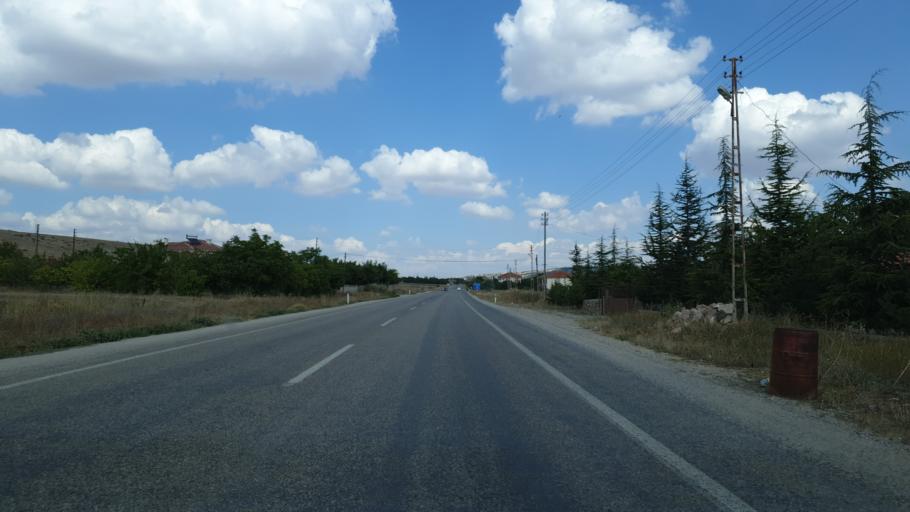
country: TR
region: Kayseri
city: Felahiye
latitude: 39.1014
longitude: 35.5883
